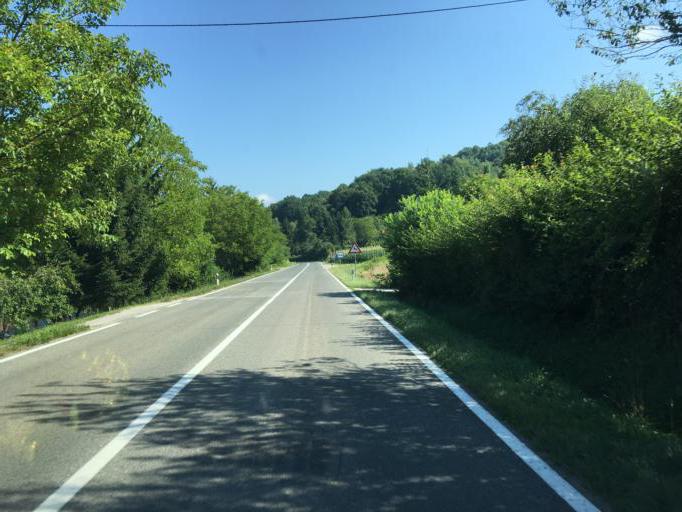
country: HR
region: Karlovacka
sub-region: Grad Karlovac
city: Karlovac
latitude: 45.4040
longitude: 15.6130
